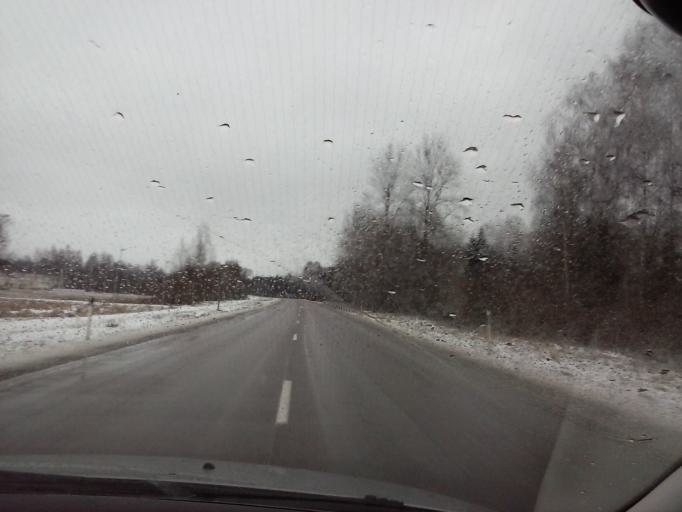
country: EE
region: Valgamaa
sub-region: Valga linn
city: Valga
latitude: 57.7967
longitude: 26.0630
